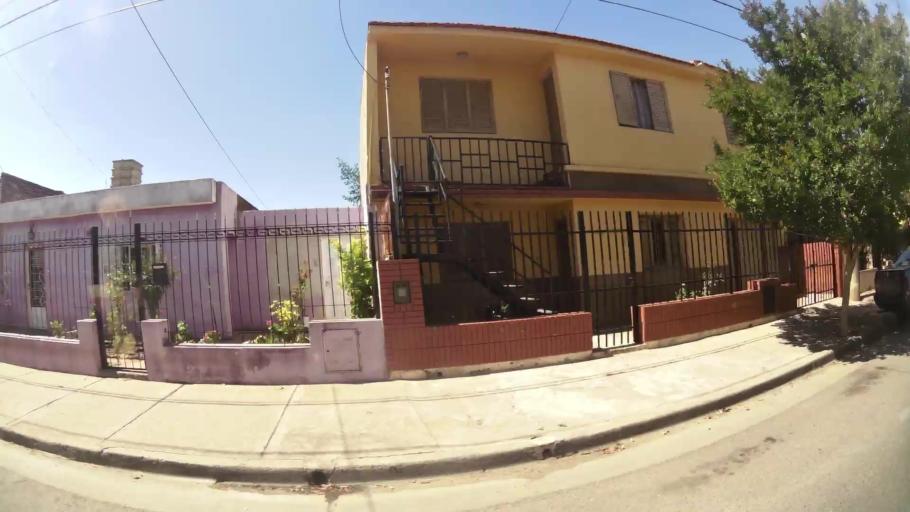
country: AR
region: Cordoba
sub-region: Departamento de Capital
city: Cordoba
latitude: -31.3780
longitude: -64.1565
